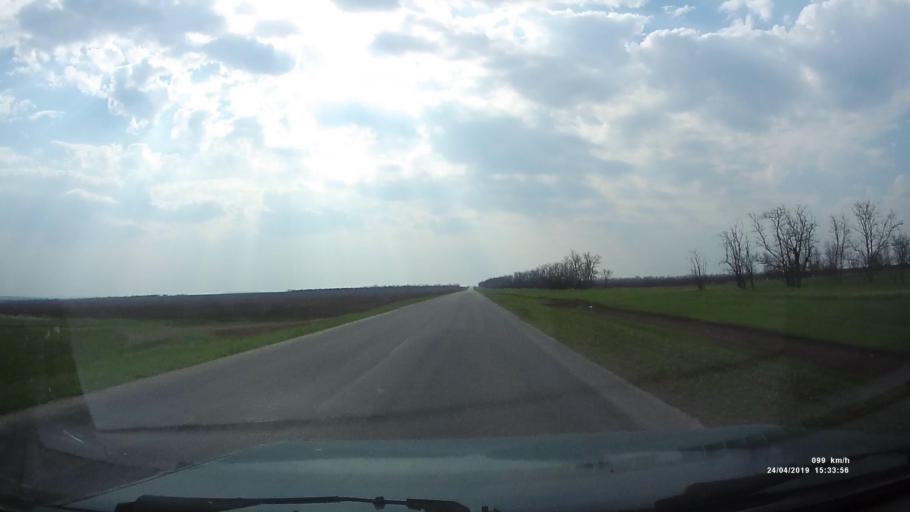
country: RU
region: Kalmykiya
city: Yashalta
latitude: 46.5996
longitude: 42.9280
